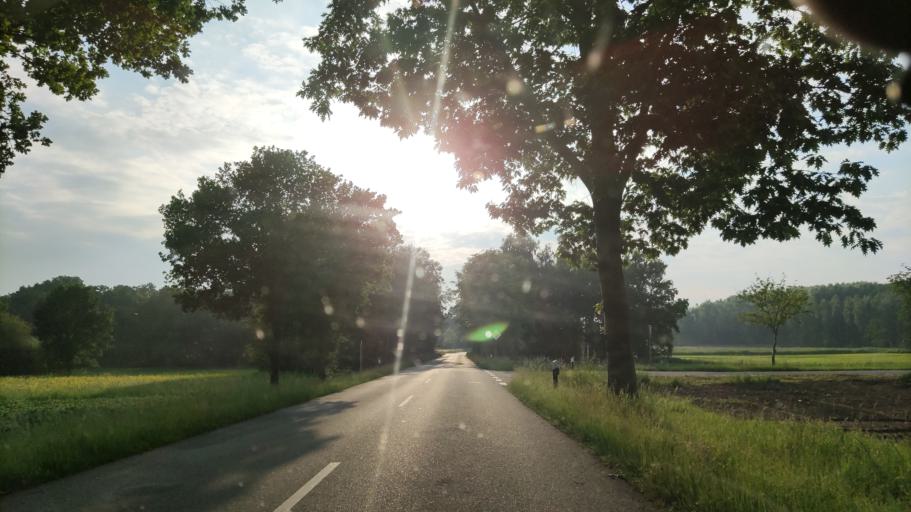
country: DE
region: Lower Saxony
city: Hanstedt Eins
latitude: 53.0319
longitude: 10.3522
